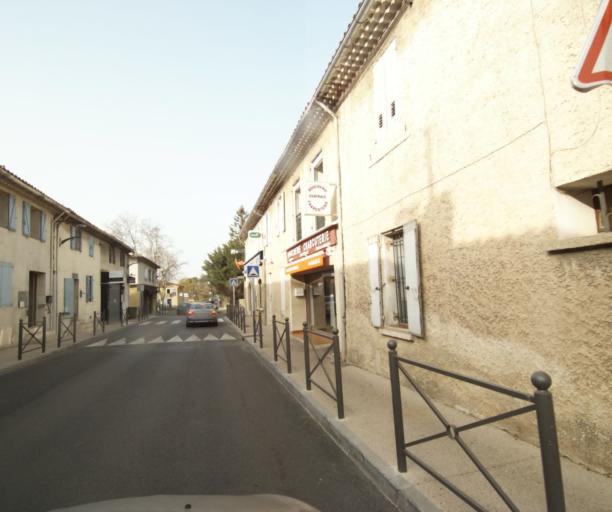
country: FR
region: Provence-Alpes-Cote d'Azur
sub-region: Departement des Bouches-du-Rhone
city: Cabries
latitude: 43.4603
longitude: 5.3532
